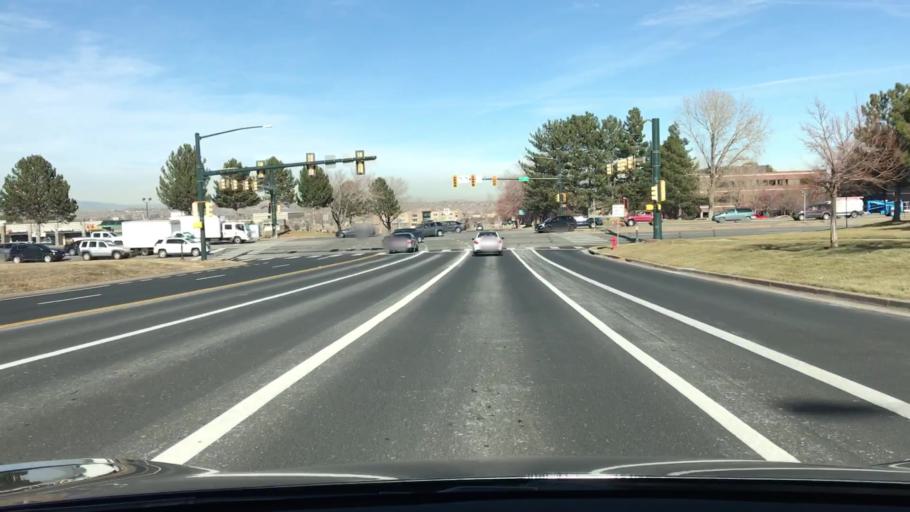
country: US
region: Colorado
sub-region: Adams County
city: Northglenn
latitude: 39.9131
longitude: -105.0060
